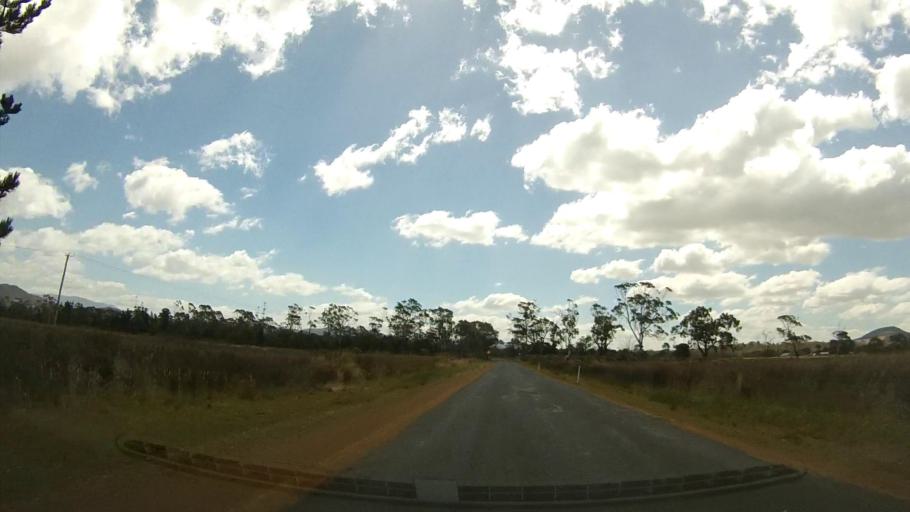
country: AU
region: Tasmania
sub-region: Clarence
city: Seven Mile Beach
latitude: -42.8319
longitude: 147.5200
